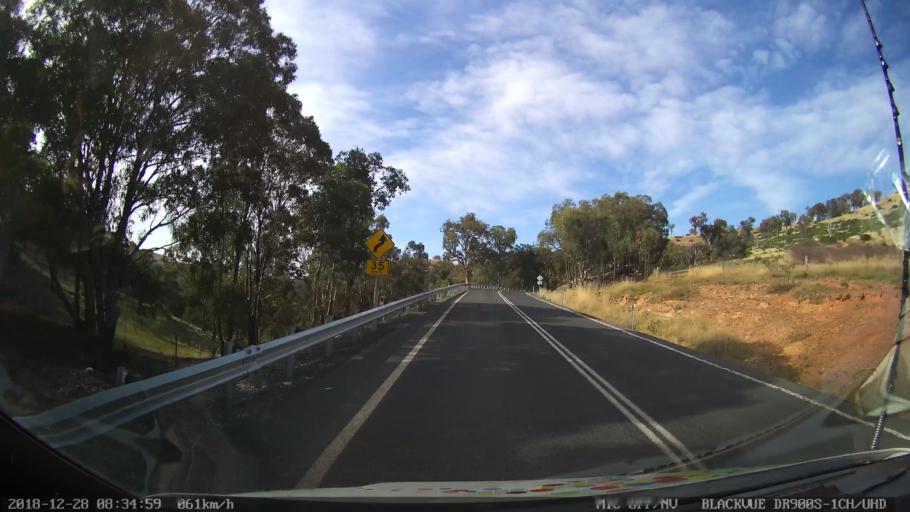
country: AU
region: New South Wales
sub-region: Blayney
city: Blayney
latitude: -33.9802
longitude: 149.3102
